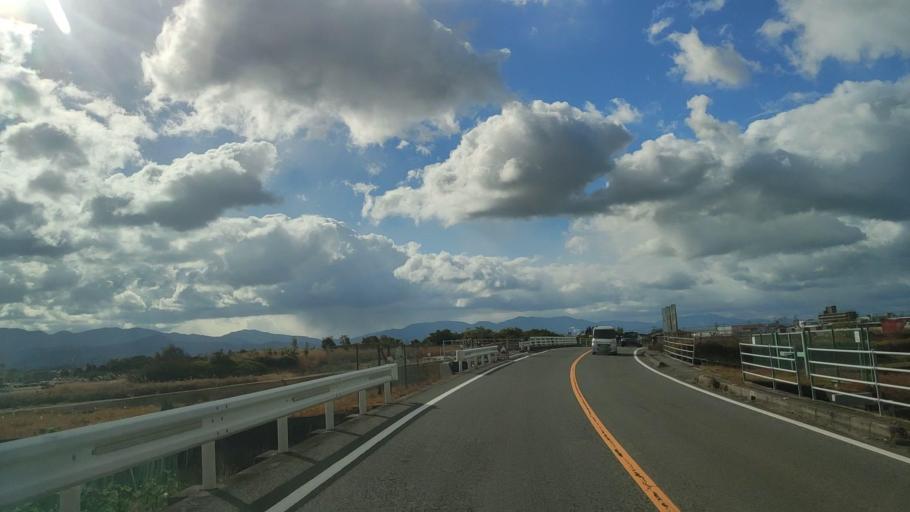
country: JP
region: Ehime
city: Masaki-cho
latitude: 33.8198
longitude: 132.7132
